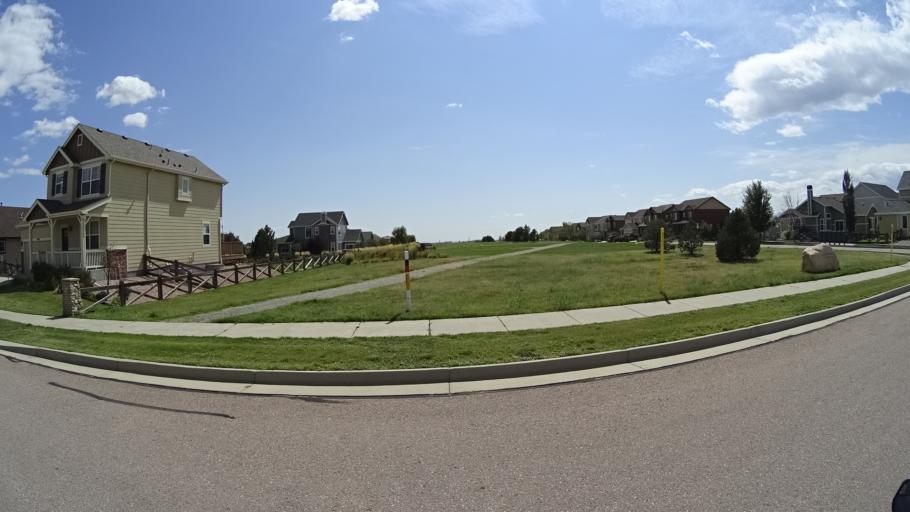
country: US
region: Colorado
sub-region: El Paso County
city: Cimarron Hills
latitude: 38.9319
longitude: -104.6808
